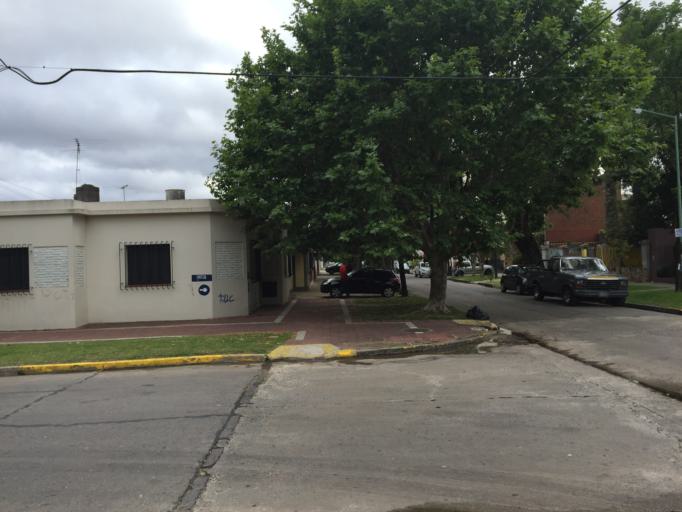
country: AR
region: Buenos Aires
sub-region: Partido de Lomas de Zamora
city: Lomas de Zamora
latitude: -34.7534
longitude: -58.3921
